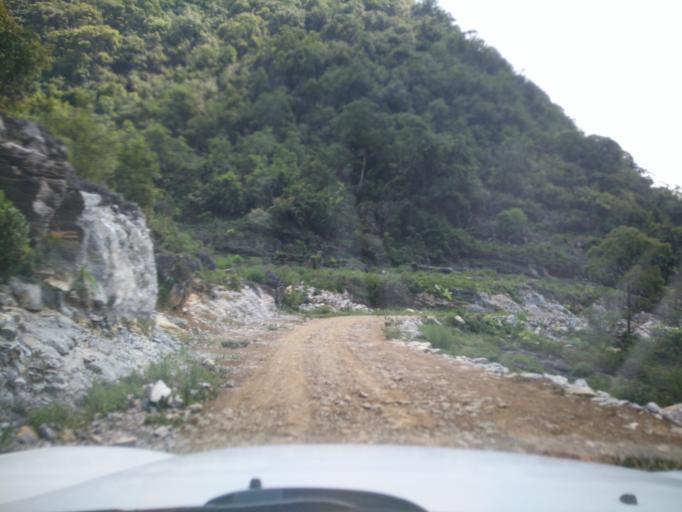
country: CN
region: Guangxi Zhuangzu Zizhiqu
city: Xinzhou
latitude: 25.1354
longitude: 105.6743
